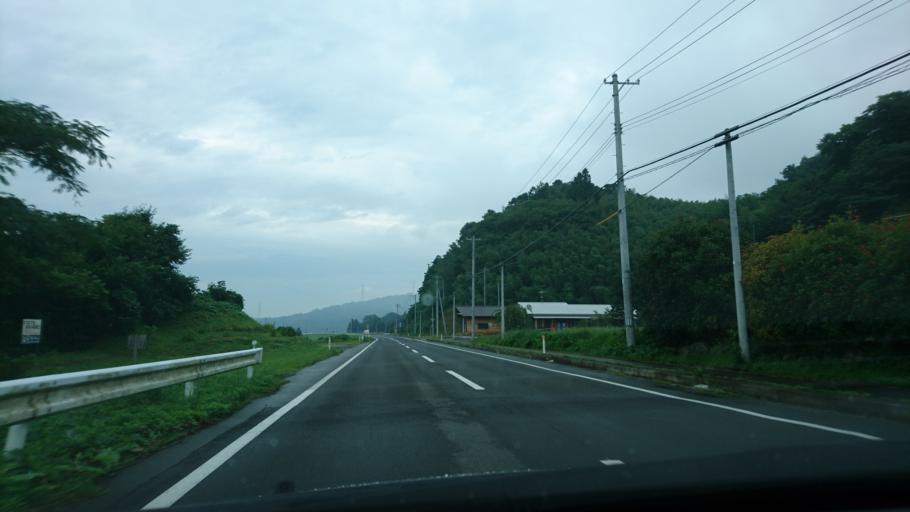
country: JP
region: Iwate
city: Ichinoseki
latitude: 38.9144
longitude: 141.2572
